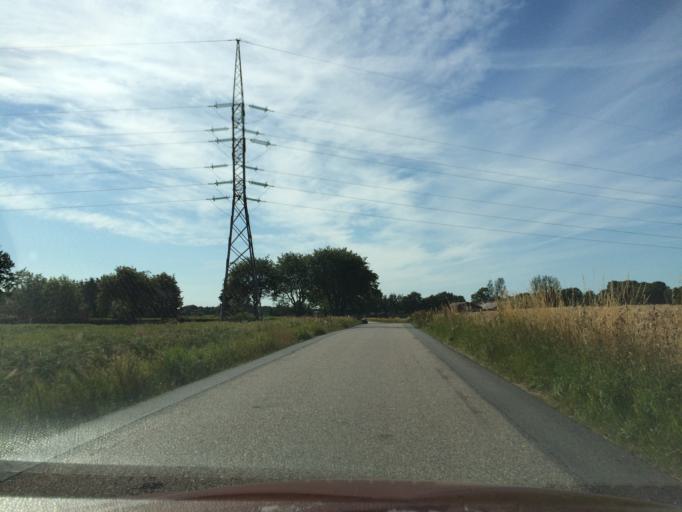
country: DK
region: Central Jutland
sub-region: Silkeborg Kommune
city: Silkeborg
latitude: 56.2233
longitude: 9.5701
